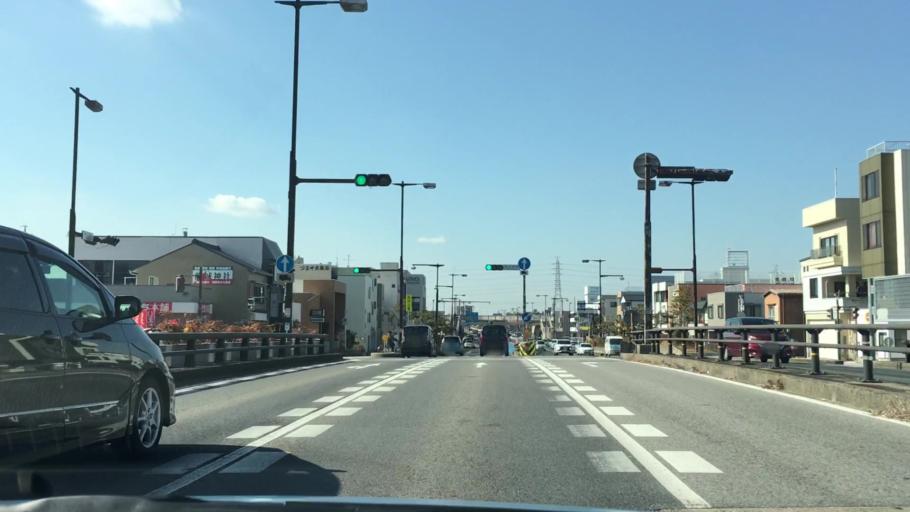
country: JP
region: Aichi
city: Okazaki
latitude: 34.9584
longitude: 137.1582
